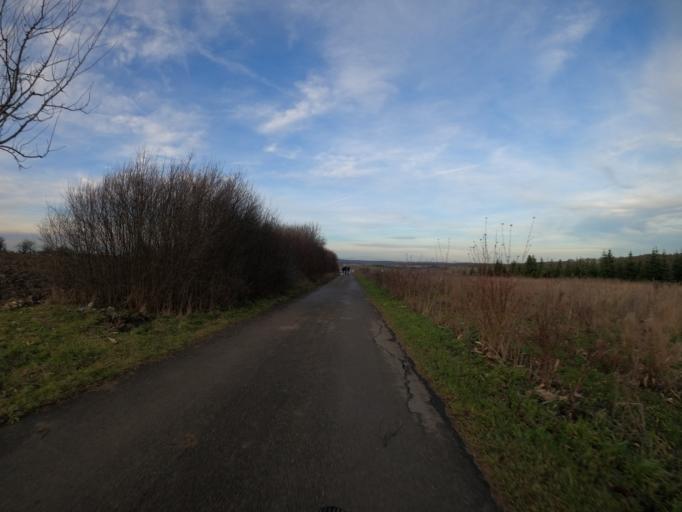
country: DE
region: Baden-Wuerttemberg
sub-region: Regierungsbezirk Stuttgart
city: Hattenhofen
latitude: 48.6577
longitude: 9.5742
